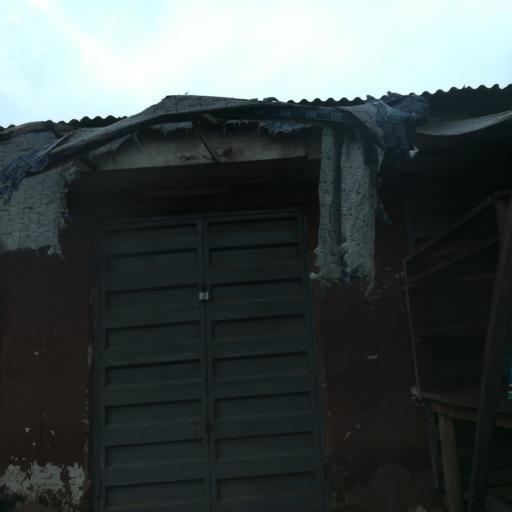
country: NG
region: Lagos
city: Agege
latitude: 6.6005
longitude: 3.3027
